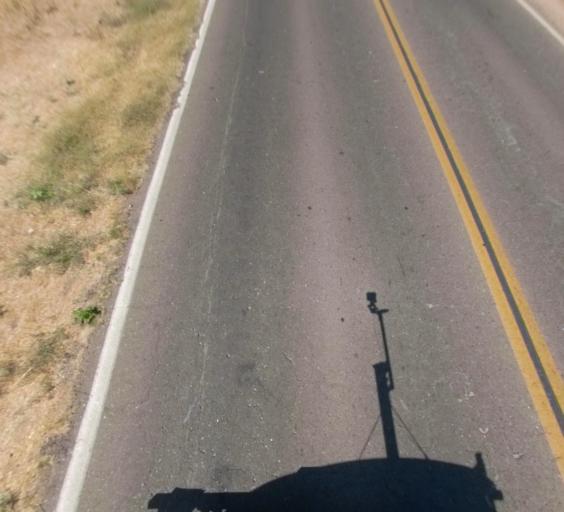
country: US
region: California
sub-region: Madera County
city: Madera
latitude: 36.9832
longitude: -120.0317
